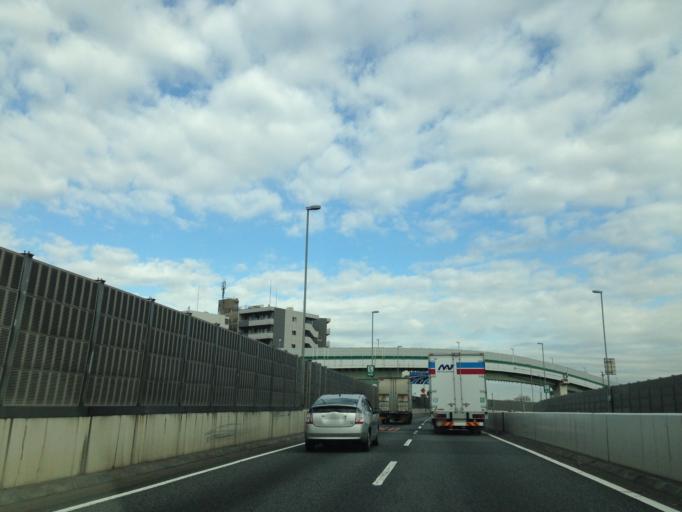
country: JP
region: Saitama
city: Kawaguchi
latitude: 35.7543
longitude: 139.7423
